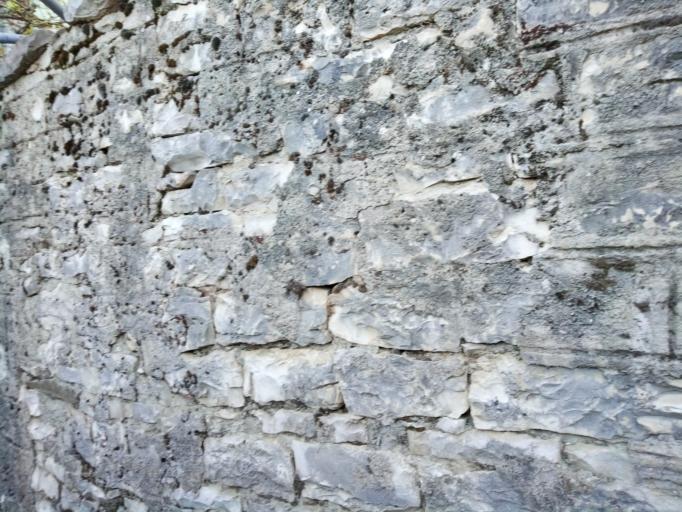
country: GR
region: Epirus
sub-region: Nomos Ioanninon
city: Asprangeloi
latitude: 39.8543
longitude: 20.7644
